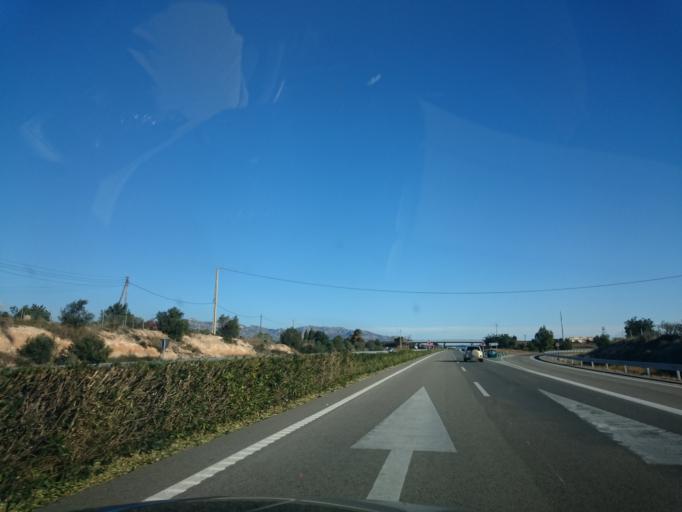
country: ES
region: Catalonia
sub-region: Provincia de Tarragona
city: l'Ametlla de Mar
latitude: 40.8819
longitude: 0.7945
